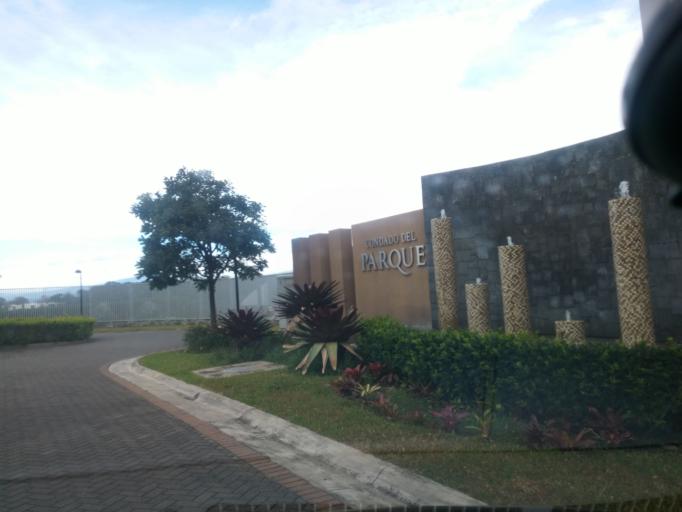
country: CR
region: San Jose
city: Colima
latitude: 9.9419
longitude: -84.0960
